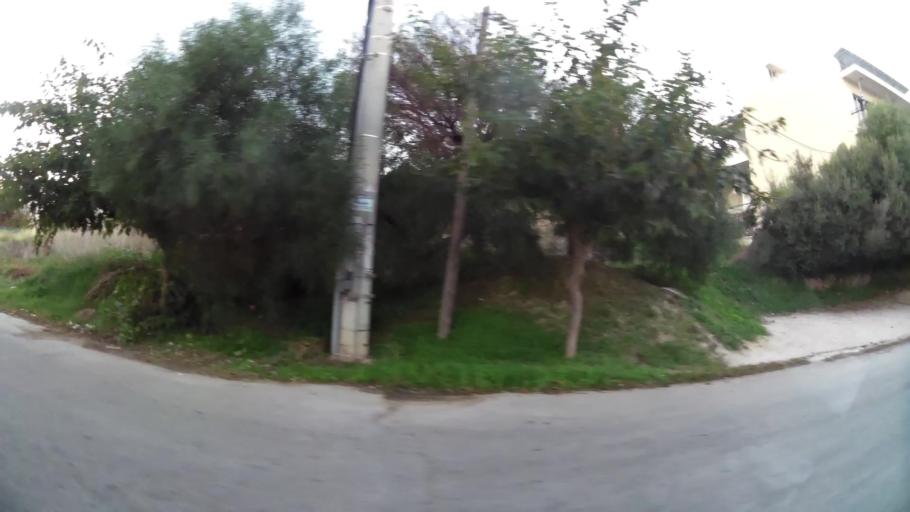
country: GR
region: Attica
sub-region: Nomarchia Anatolikis Attikis
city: Spata
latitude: 37.9663
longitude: 23.9138
